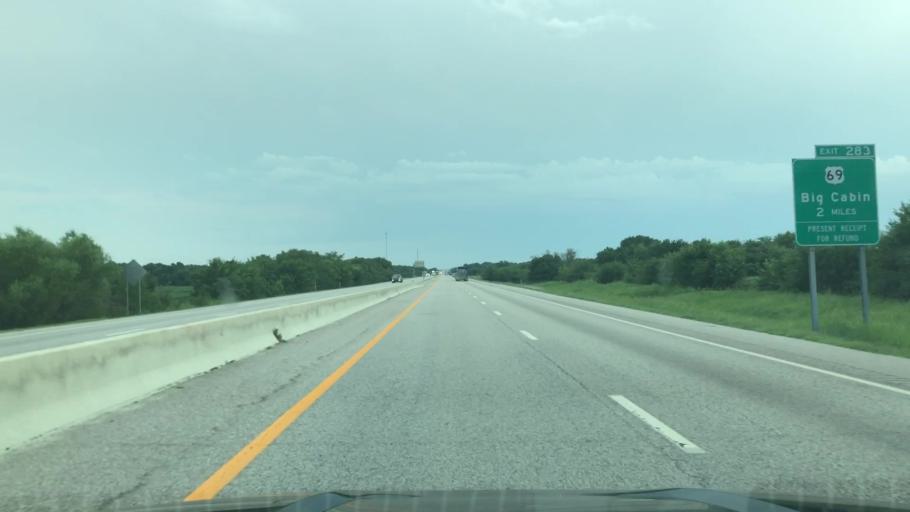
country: US
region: Oklahoma
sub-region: Craig County
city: Vinita
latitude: 36.5951
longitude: -95.1945
